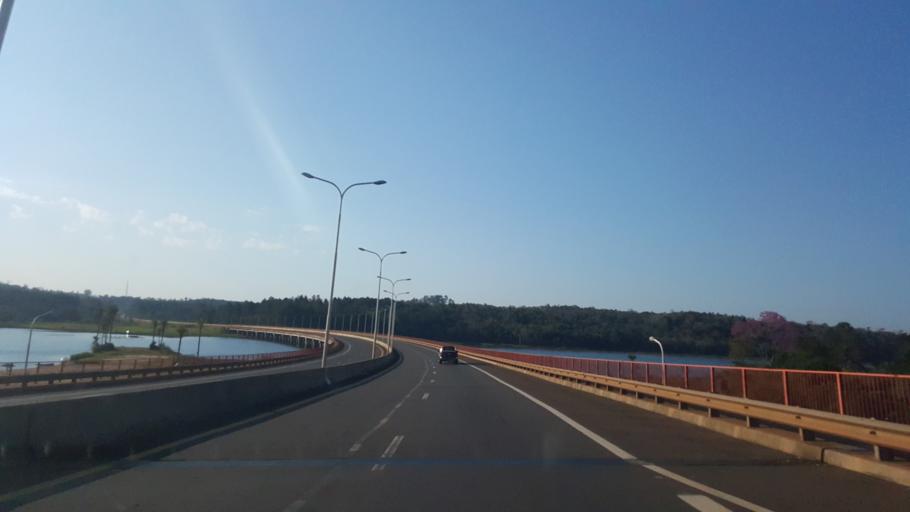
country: AR
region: Misiones
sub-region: Departamento de San Ignacio
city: San Ignacio
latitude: -27.2889
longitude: -55.5330
